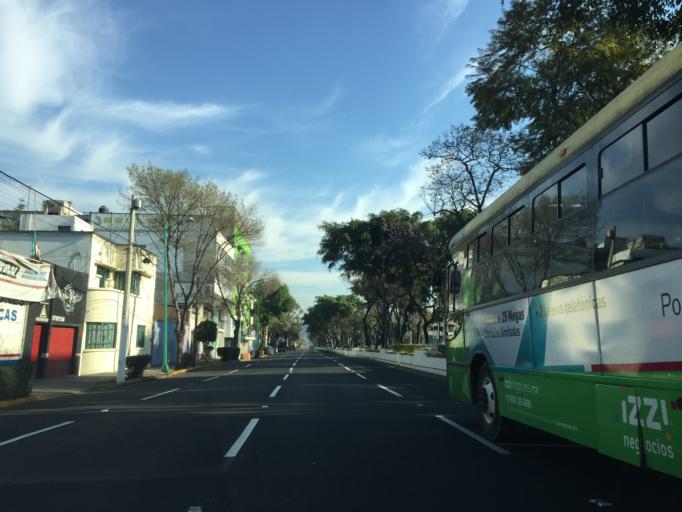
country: MX
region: Mexico
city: Colonia Lindavista
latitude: 19.4735
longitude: -99.1217
